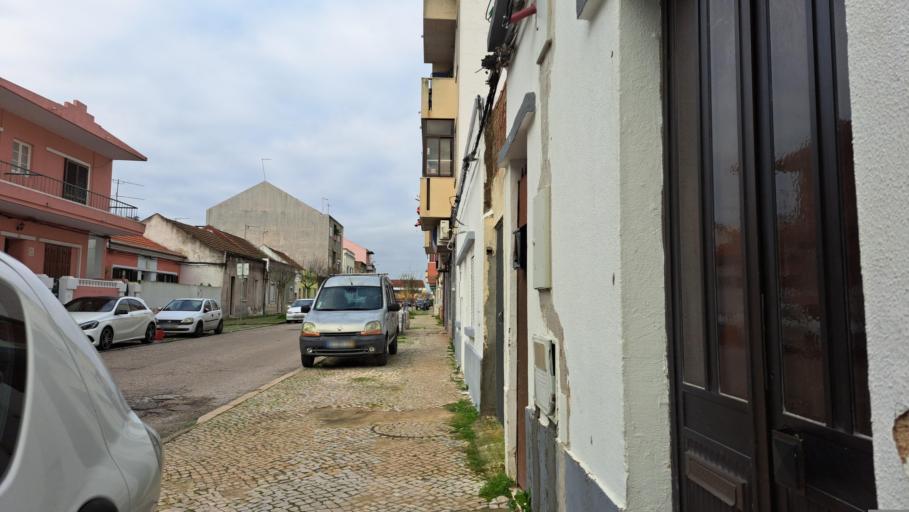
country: PT
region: Setubal
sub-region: Moita
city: Alhos Vedros
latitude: 38.6591
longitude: -9.0479
